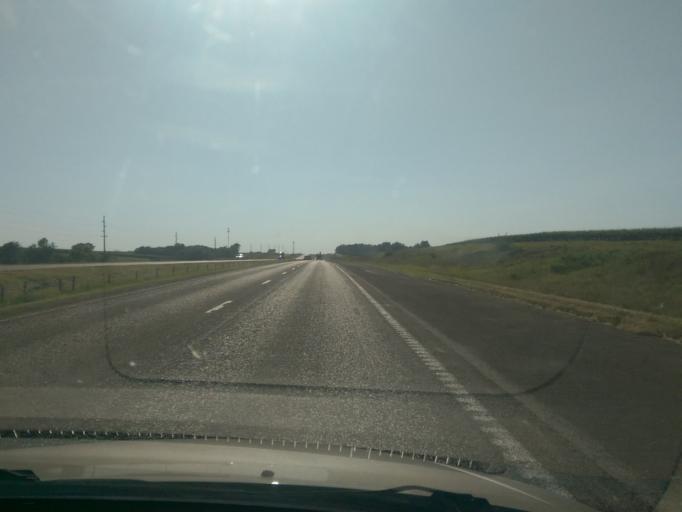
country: US
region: Missouri
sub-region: Lafayette County
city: Concordia
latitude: 38.9919
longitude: -93.6530
